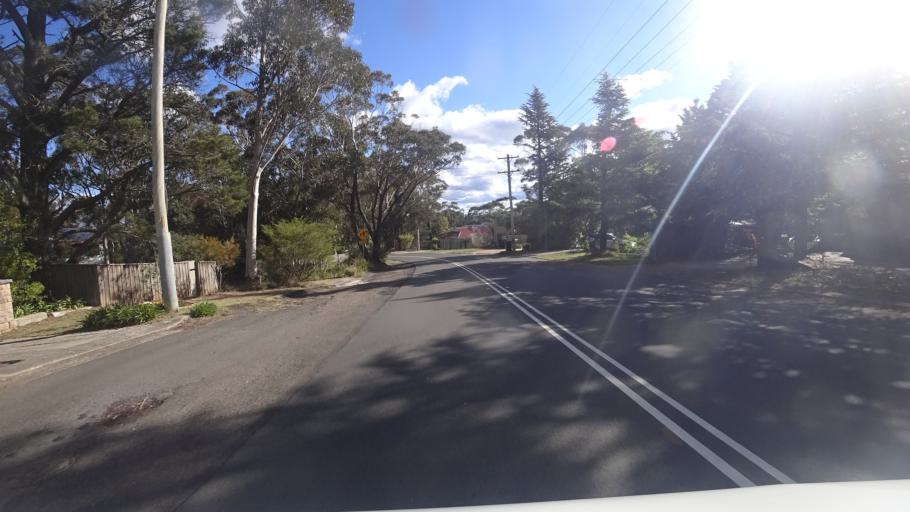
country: AU
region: New South Wales
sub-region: Blue Mountains Municipality
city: Katoomba
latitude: -33.7187
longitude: 150.2942
